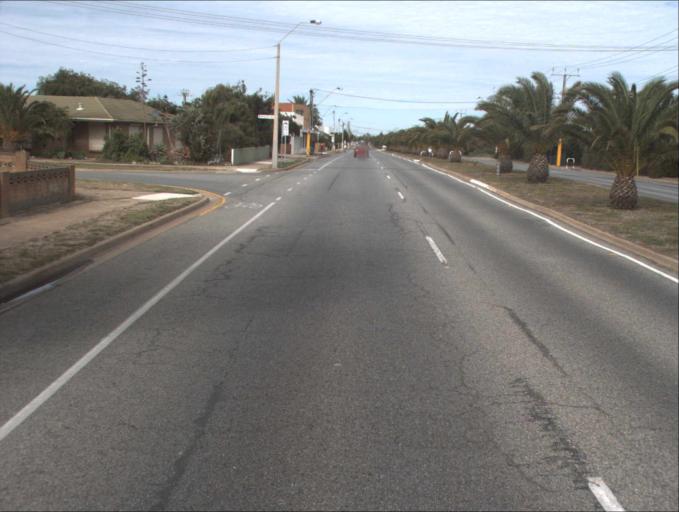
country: AU
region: South Australia
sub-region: Charles Sturt
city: West Lakes Shore
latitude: -34.8597
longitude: 138.4790
